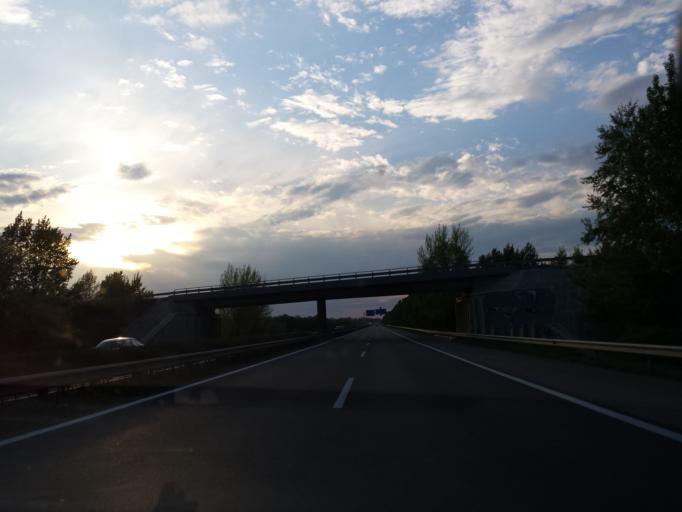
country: HU
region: Gyor-Moson-Sopron
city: Abda
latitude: 47.6686
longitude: 17.5683
